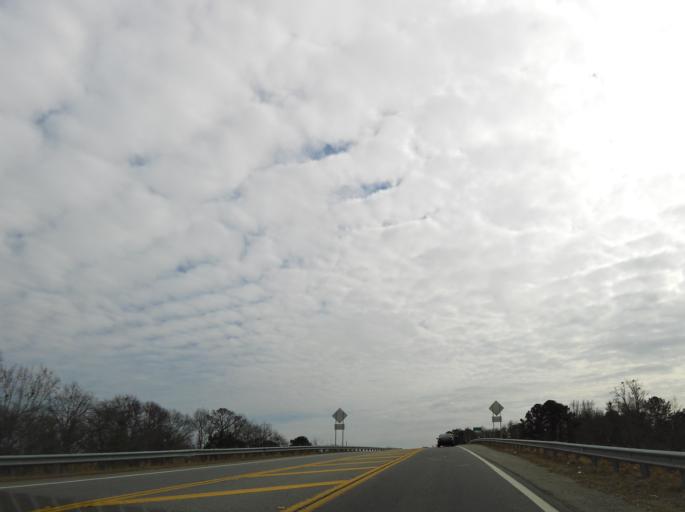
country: US
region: Georgia
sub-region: Peach County
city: Byron
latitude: 32.6507
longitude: -83.7633
